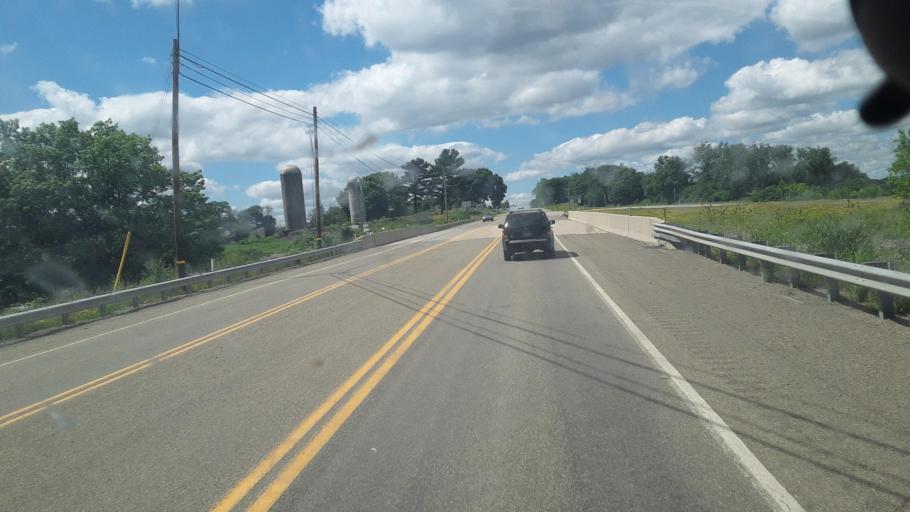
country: US
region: Pennsylvania
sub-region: Butler County
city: Prospect
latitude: 40.9671
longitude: -80.1617
